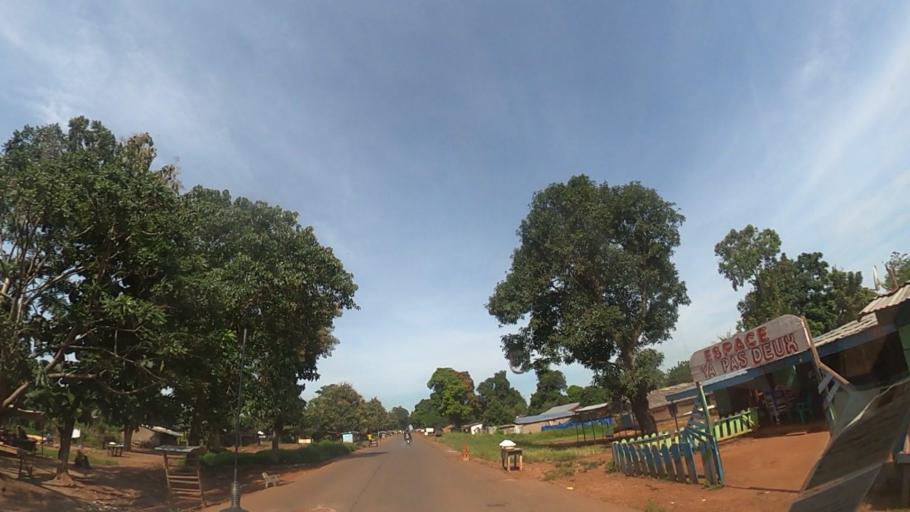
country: CF
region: Ombella-Mpoko
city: Bimbo
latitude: 4.3118
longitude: 18.4801
